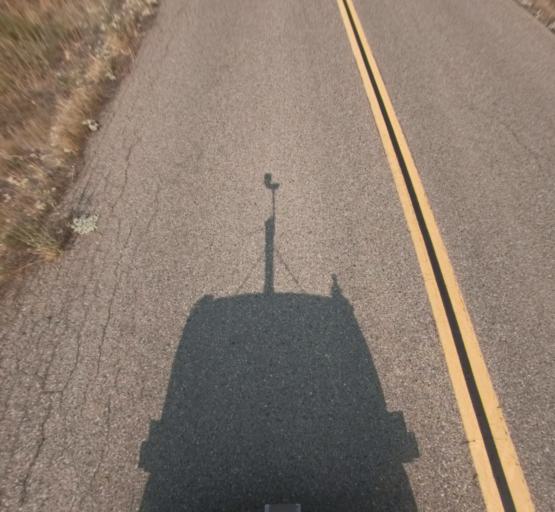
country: US
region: California
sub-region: Madera County
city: Madera Acres
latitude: 37.1193
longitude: -119.9649
